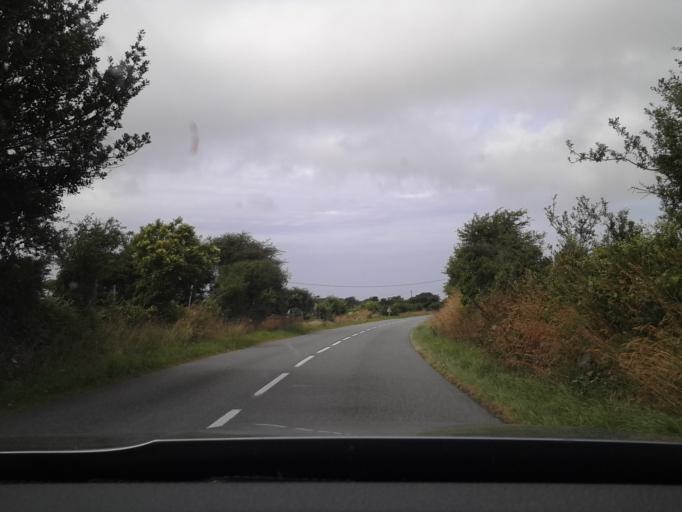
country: FR
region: Lower Normandy
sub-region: Departement de la Manche
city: Beaumont-Hague
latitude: 49.6782
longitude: -1.8370
